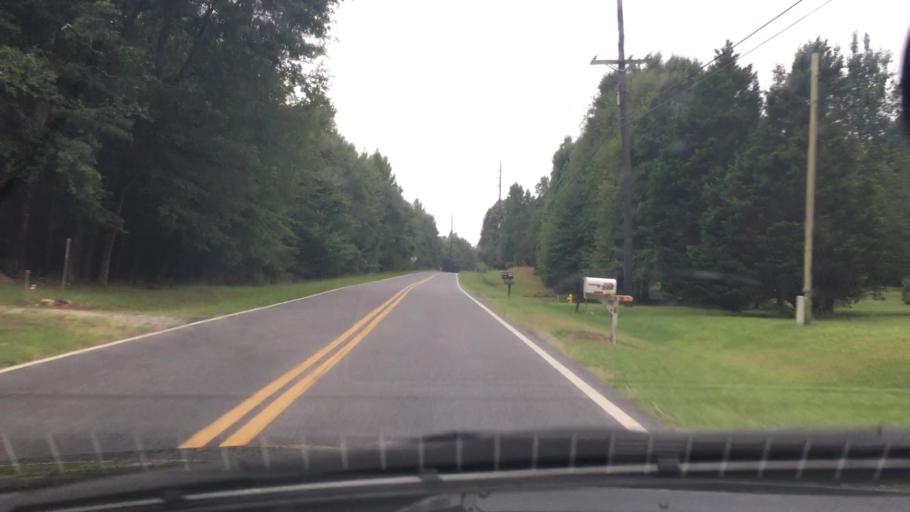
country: US
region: Georgia
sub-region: Spalding County
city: Experiment
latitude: 33.2558
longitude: -84.3886
